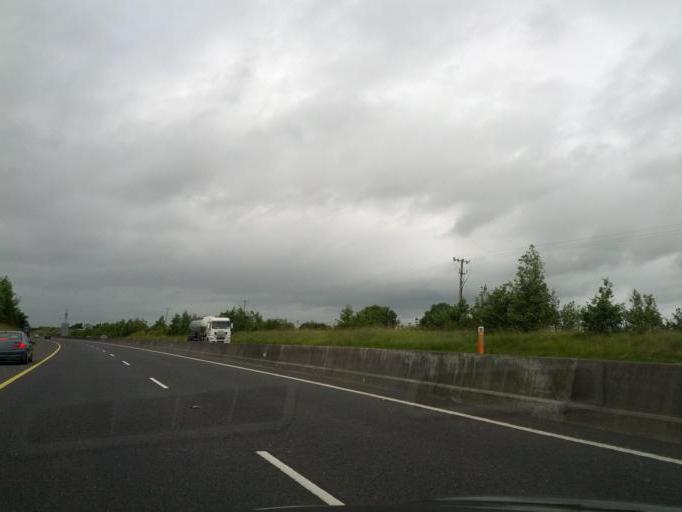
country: IE
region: Munster
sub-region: An Clar
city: Newmarket on Fergus
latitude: 52.7982
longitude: -8.9227
